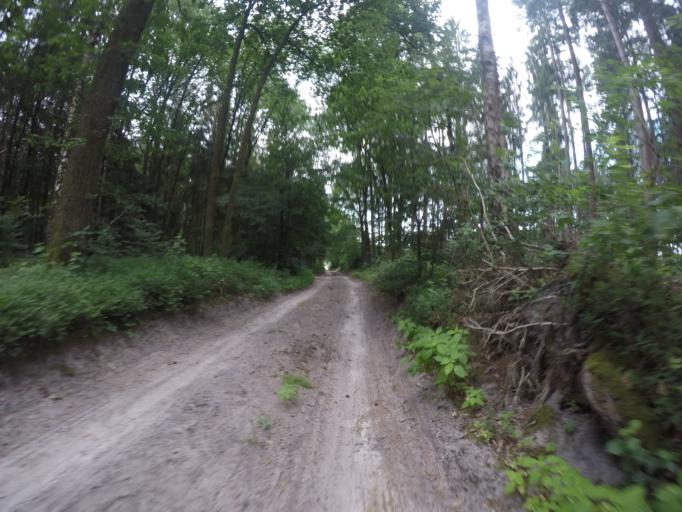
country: DE
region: Lower Saxony
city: Undeloh
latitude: 53.2043
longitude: 9.9762
